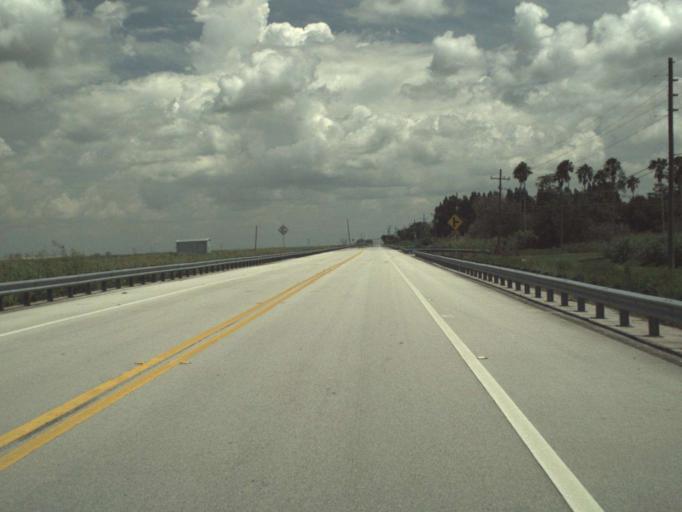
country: US
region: Florida
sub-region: Palm Beach County
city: Pahokee
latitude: 26.8533
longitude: -80.6173
